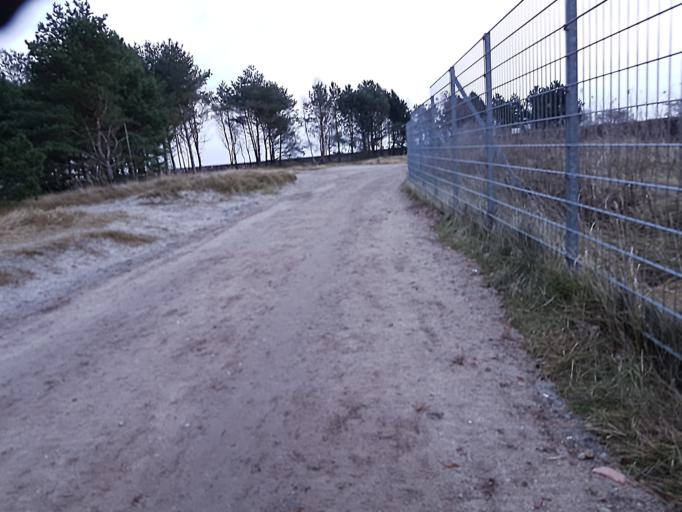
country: DE
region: Mecklenburg-Vorpommern
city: Ostseebad Binz
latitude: 54.4399
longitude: 13.5763
